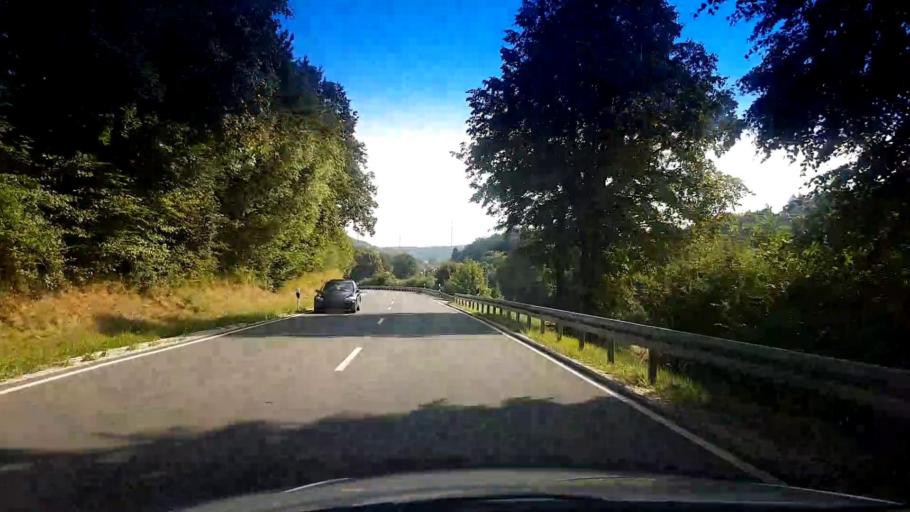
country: DE
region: Bavaria
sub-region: Upper Franconia
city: Glashutten
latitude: 49.9350
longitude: 11.3914
